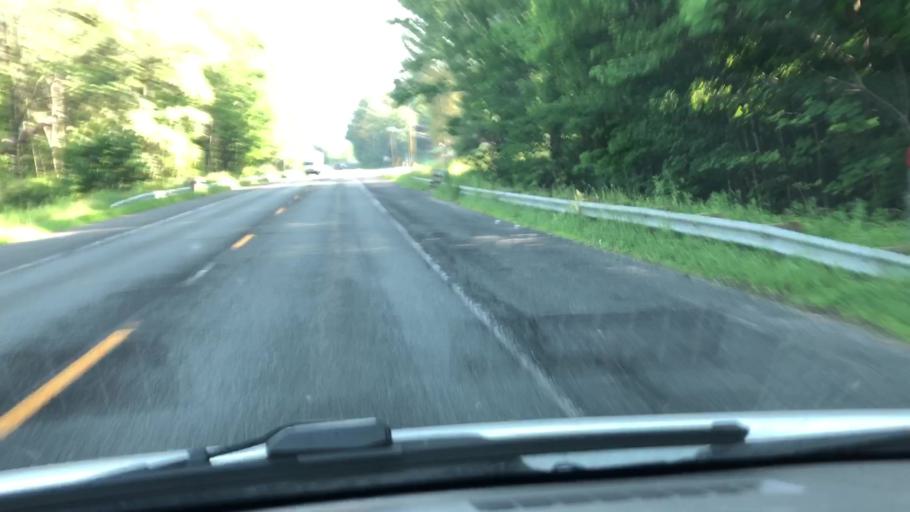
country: US
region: Massachusetts
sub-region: Berkshire County
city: Lanesborough
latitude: 42.5242
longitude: -73.1919
